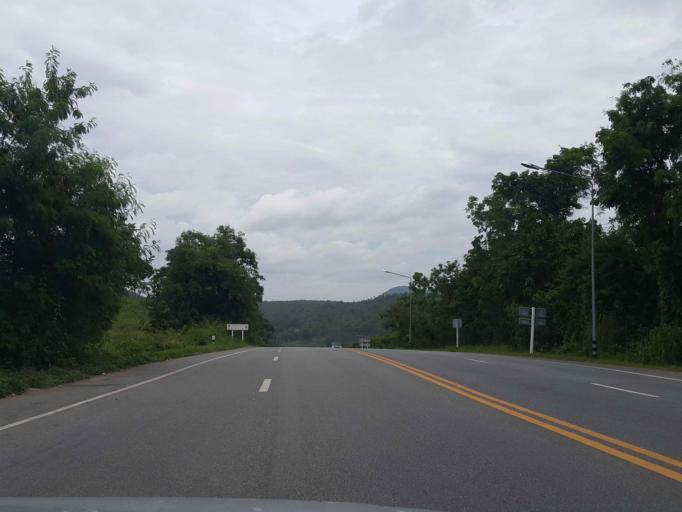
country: TH
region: Lamphun
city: Li
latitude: 17.7092
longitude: 99.0582
